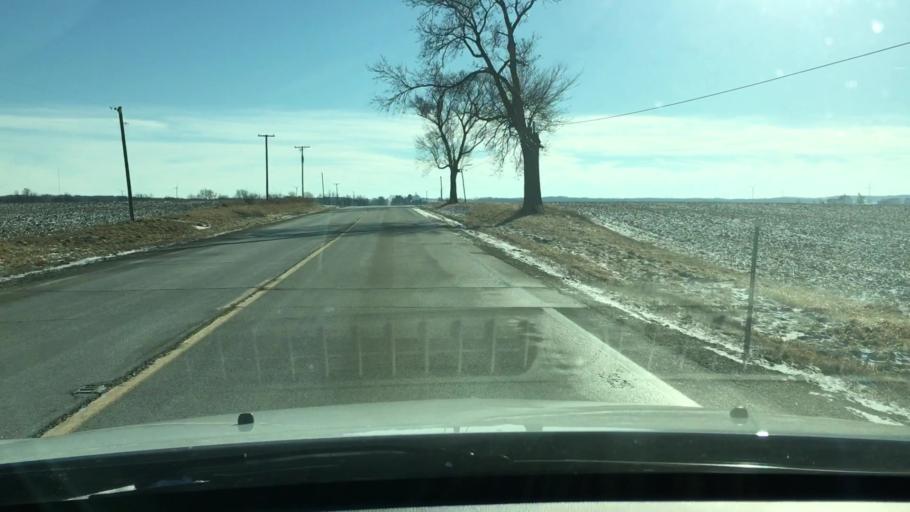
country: US
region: Illinois
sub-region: Ogle County
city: Rochelle
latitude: 41.7553
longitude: -89.0837
